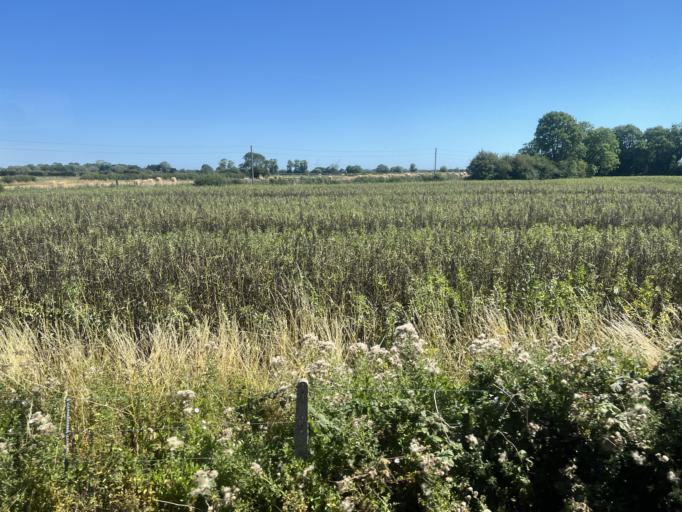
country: GB
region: England
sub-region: Lincolnshire
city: Wainfleet All Saints
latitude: 53.1318
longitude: 0.1924
